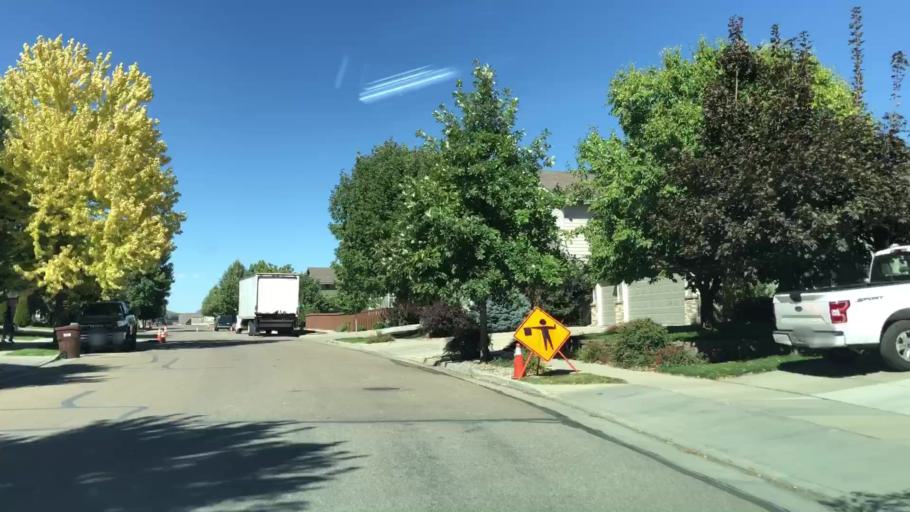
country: US
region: Colorado
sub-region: Larimer County
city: Fort Collins
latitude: 40.5007
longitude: -105.0339
